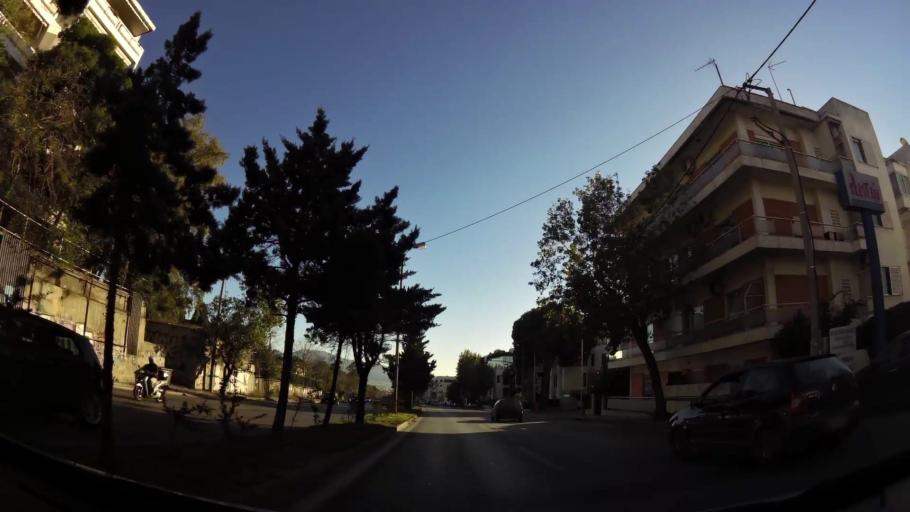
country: GR
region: Attica
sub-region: Nomarchia Athinas
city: Kifisia
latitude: 38.0656
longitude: 23.8096
